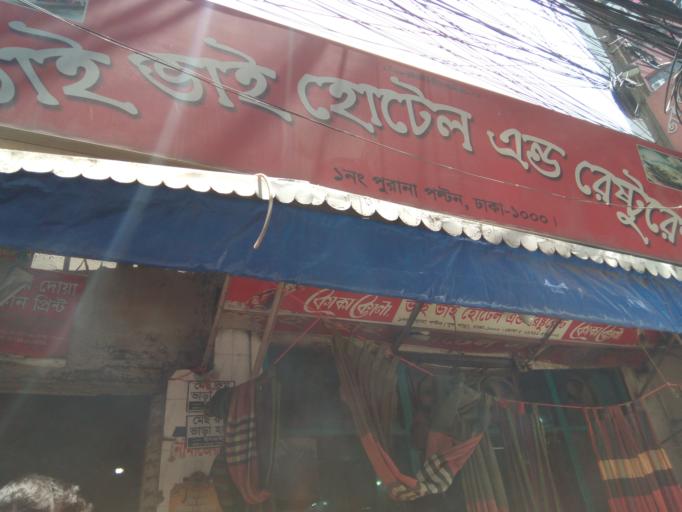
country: BD
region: Dhaka
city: Paltan
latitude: 23.7328
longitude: 90.4116
